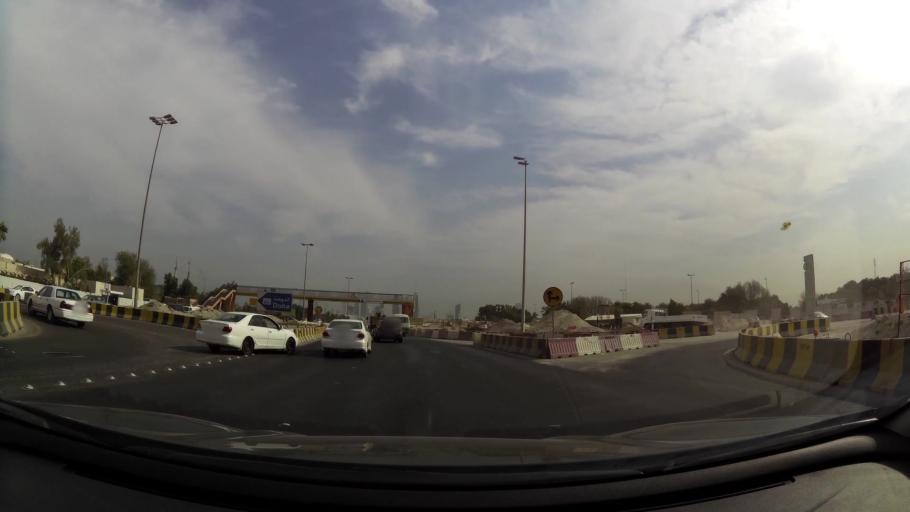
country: KW
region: Al Asimah
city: Ash Shamiyah
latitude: 29.3508
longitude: 47.9441
